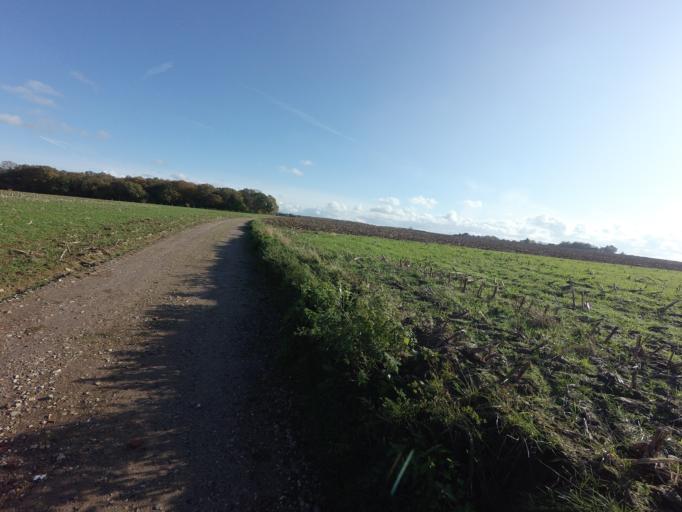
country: NL
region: Limburg
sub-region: Eijsden-Margraten
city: Margraten
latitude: 50.7841
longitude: 5.8698
